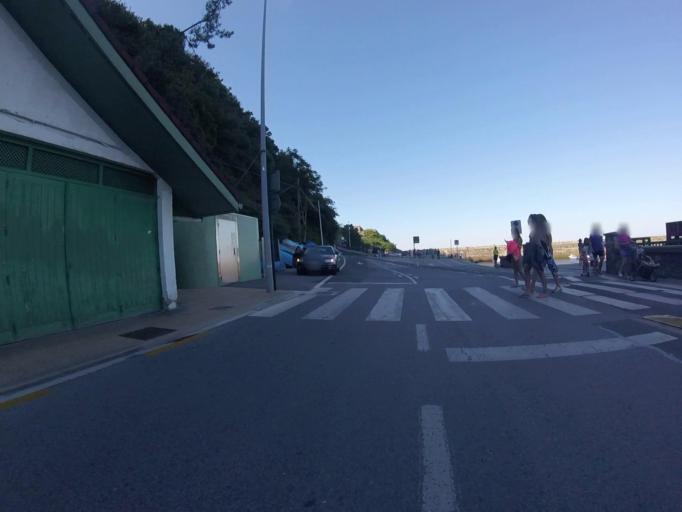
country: ES
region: Basque Country
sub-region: Provincia de Guipuzcoa
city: Fuenterrabia
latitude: 43.3878
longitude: -1.7913
